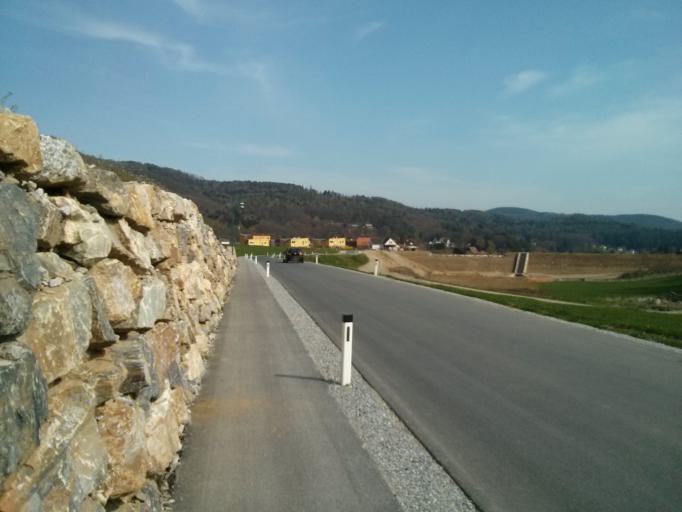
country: AT
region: Styria
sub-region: Politischer Bezirk Graz-Umgebung
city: Stattegg
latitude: 47.1381
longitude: 15.4141
